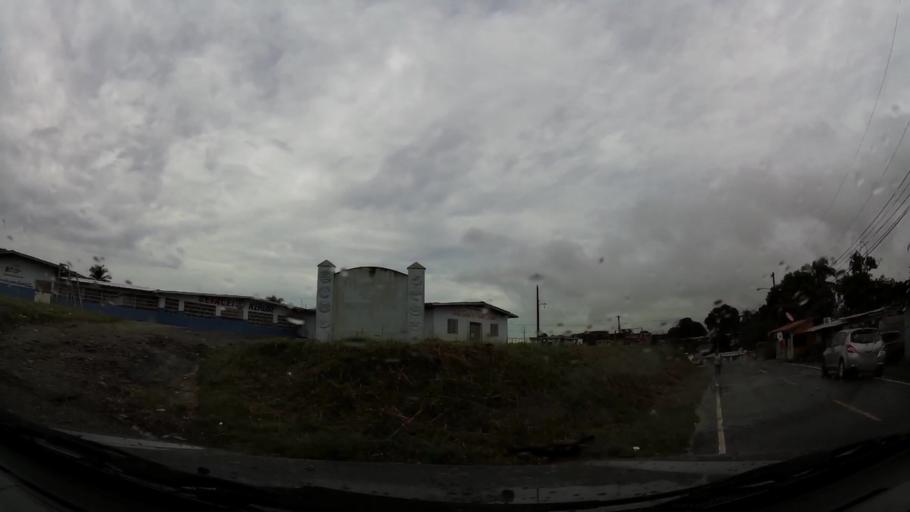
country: PA
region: Colon
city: Arco Iris
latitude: 9.3370
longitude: -79.8695
